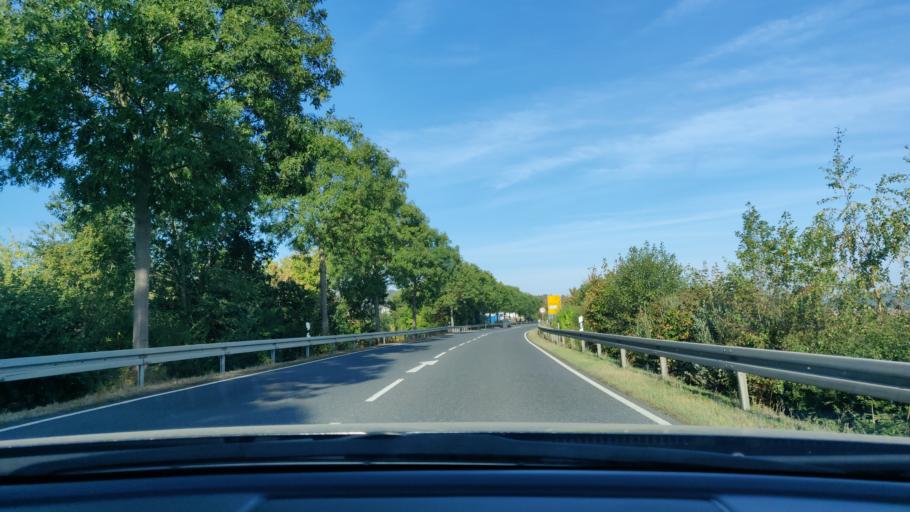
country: DE
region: Hesse
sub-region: Regierungsbezirk Kassel
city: Bad Wildungen
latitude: 51.1321
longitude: 9.1269
